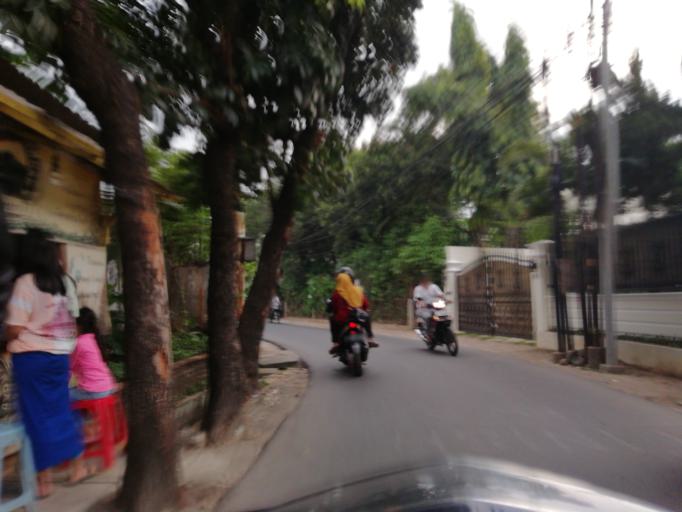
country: ID
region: West Java
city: Depok
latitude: -6.3303
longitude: 106.8209
